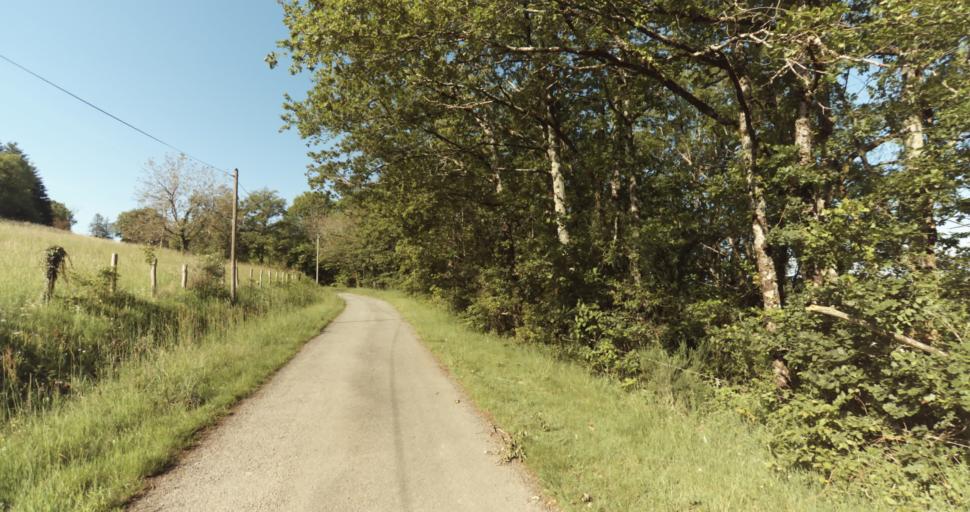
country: FR
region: Limousin
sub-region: Departement de la Haute-Vienne
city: Solignac
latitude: 45.7345
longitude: 1.2440
